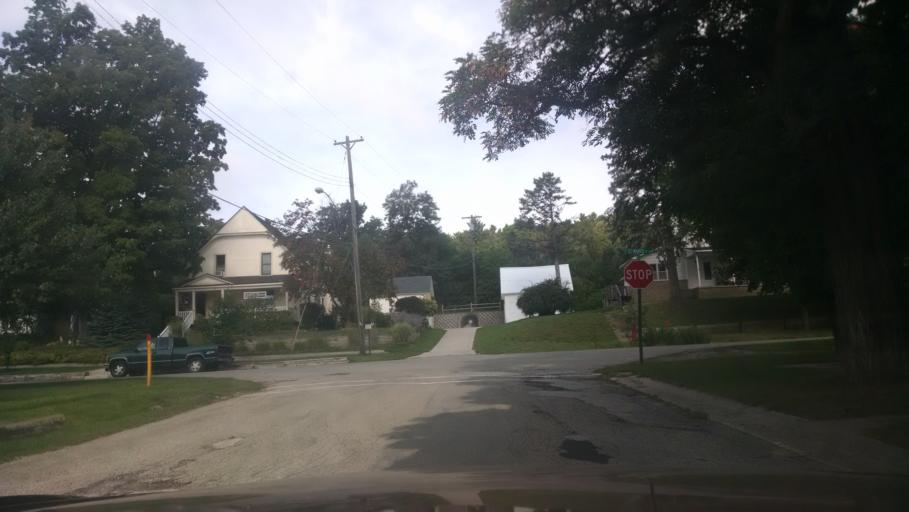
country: US
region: Michigan
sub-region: Leelanau County
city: Leland
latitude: 44.9792
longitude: -85.6500
